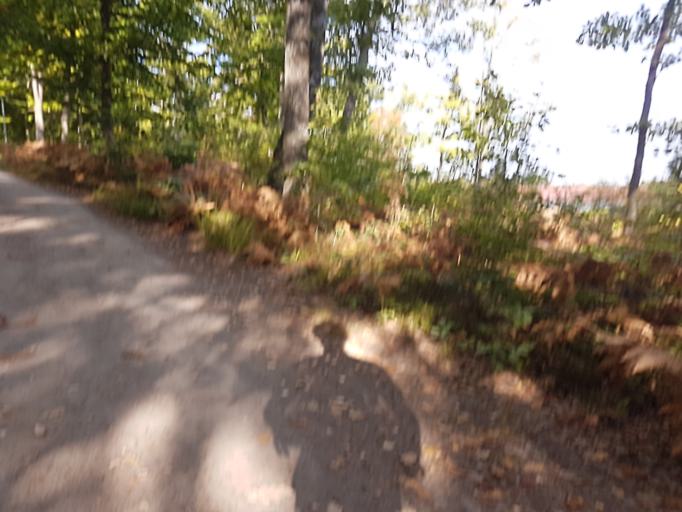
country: SE
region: Kronoberg
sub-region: Vaxjo Kommun
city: Vaexjoe
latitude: 56.8576
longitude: 14.8348
